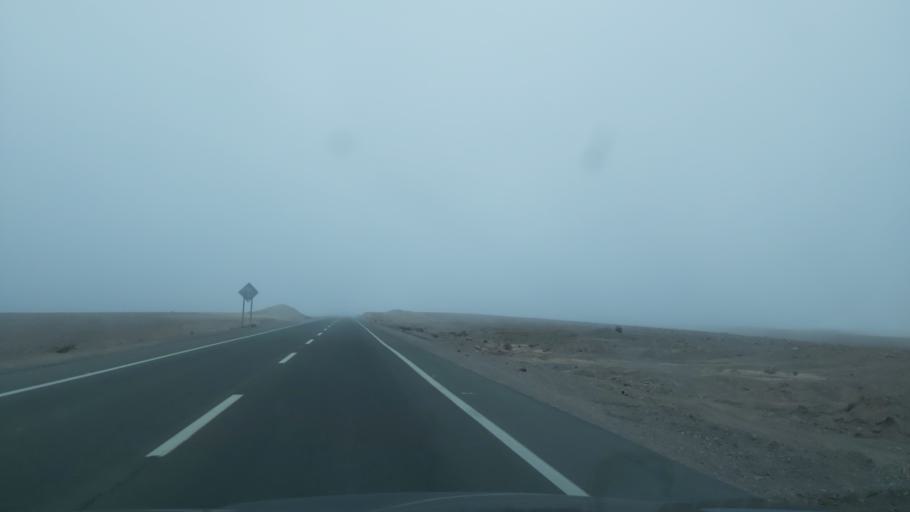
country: CL
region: Atacama
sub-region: Provincia de Copiapo
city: Copiapo
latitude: -27.2776
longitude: -70.0851
